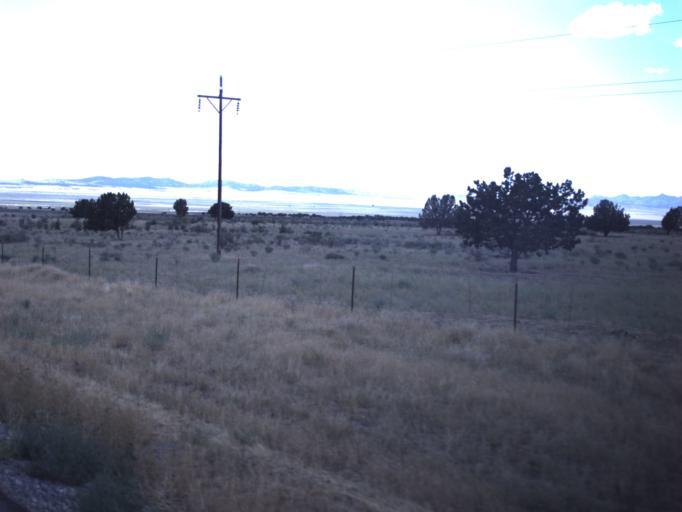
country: US
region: Utah
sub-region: Tooele County
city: Grantsville
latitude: 40.3065
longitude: -112.6423
